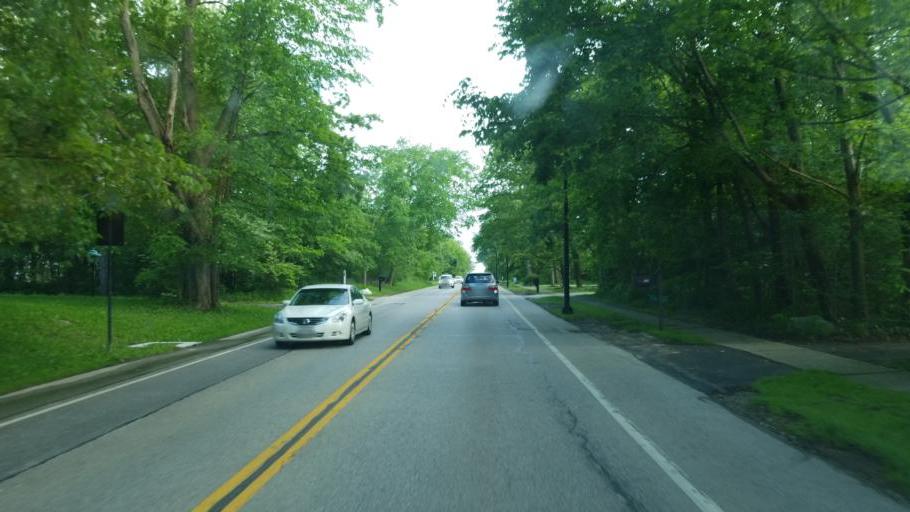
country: US
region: Ohio
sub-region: Summit County
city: Hudson
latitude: 41.2330
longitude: -81.4405
